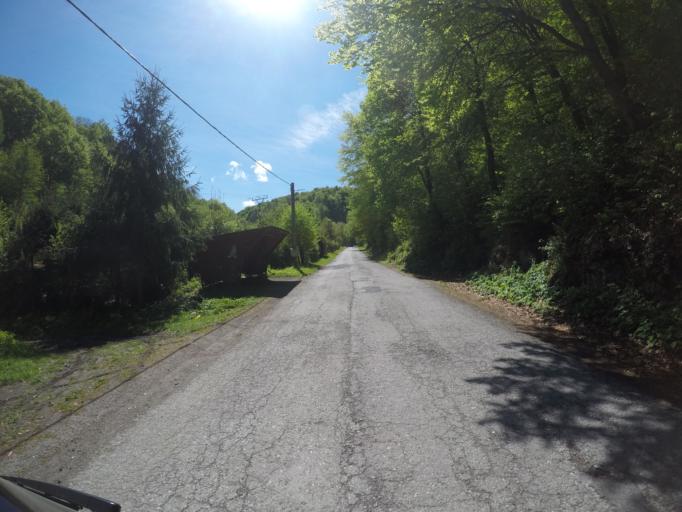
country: SK
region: Banskobystricky
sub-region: Okres Banska Bystrica
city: Banska Bystrica
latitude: 48.7261
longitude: 19.2134
